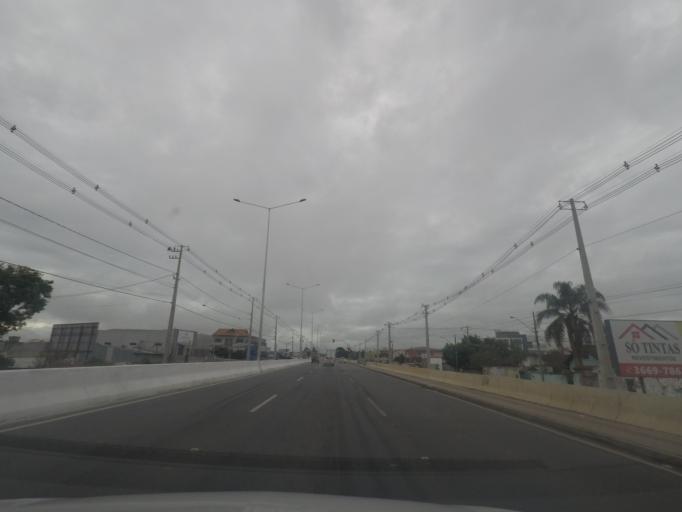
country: BR
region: Parana
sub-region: Pinhais
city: Pinhais
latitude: -25.4395
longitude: -49.1579
